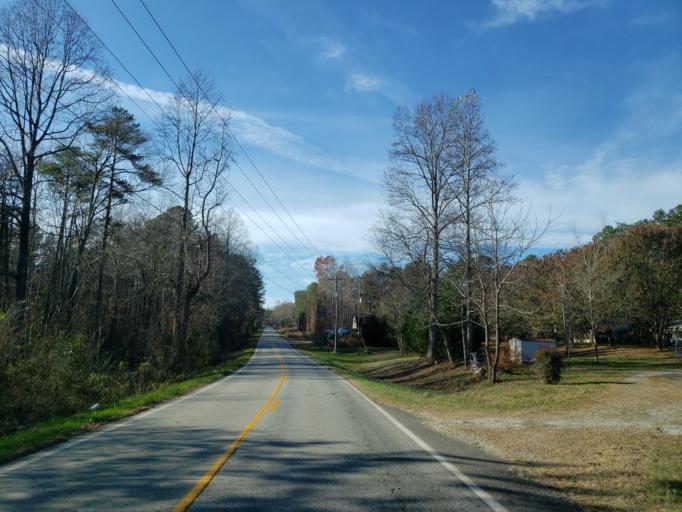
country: US
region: Georgia
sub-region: Lumpkin County
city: Dahlonega
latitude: 34.4630
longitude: -84.0061
